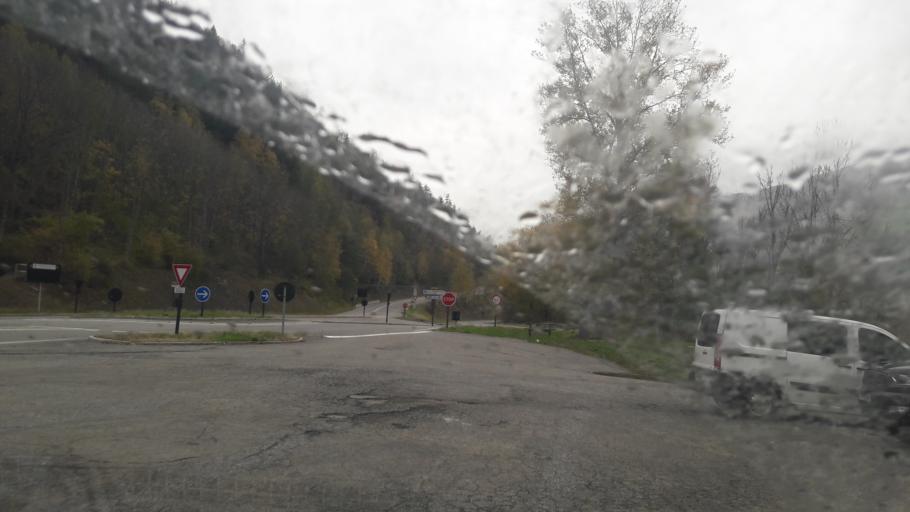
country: FR
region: Rhone-Alpes
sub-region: Departement de la Savoie
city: Seez
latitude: 45.6183
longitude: 6.7887
